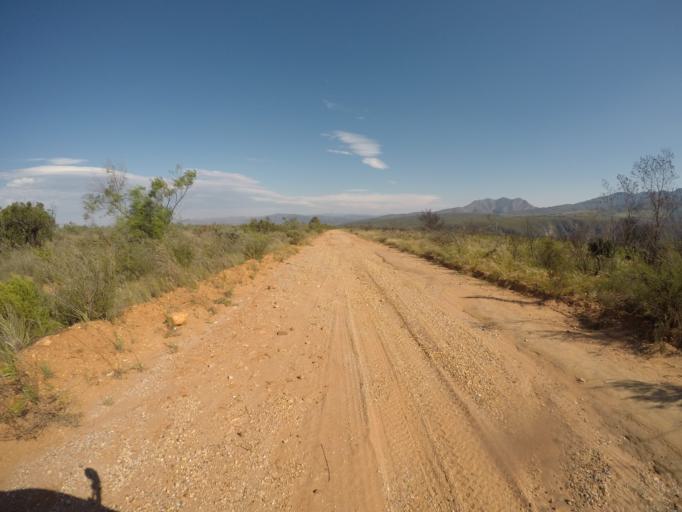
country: ZA
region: Eastern Cape
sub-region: Cacadu District Municipality
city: Kareedouw
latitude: -33.6364
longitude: 24.4585
